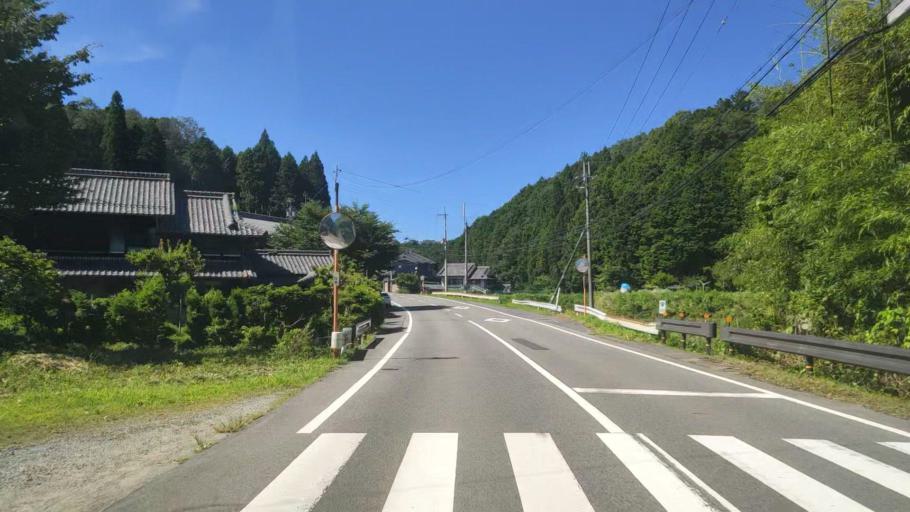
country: JP
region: Nara
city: Haibara-akanedai
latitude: 34.4526
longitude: 135.9365
